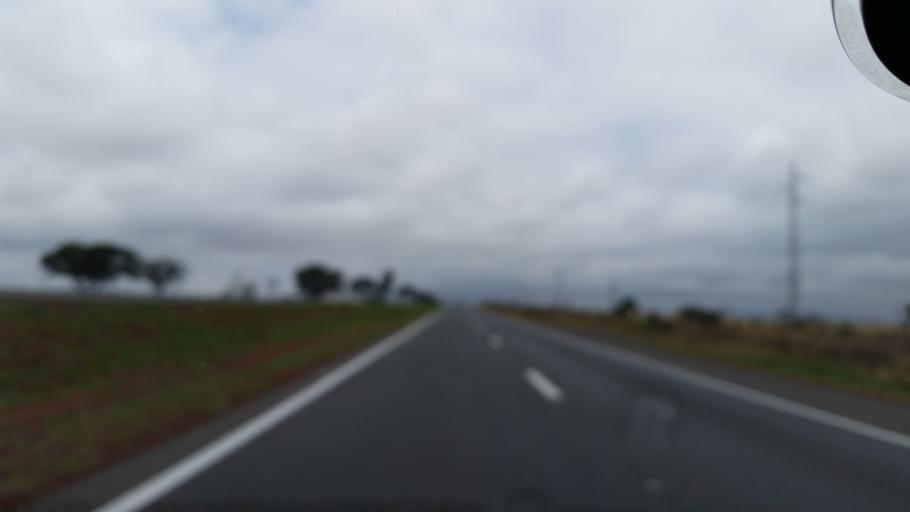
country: BR
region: Goias
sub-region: Cristalina
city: Cristalina
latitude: -16.6935
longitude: -47.6969
